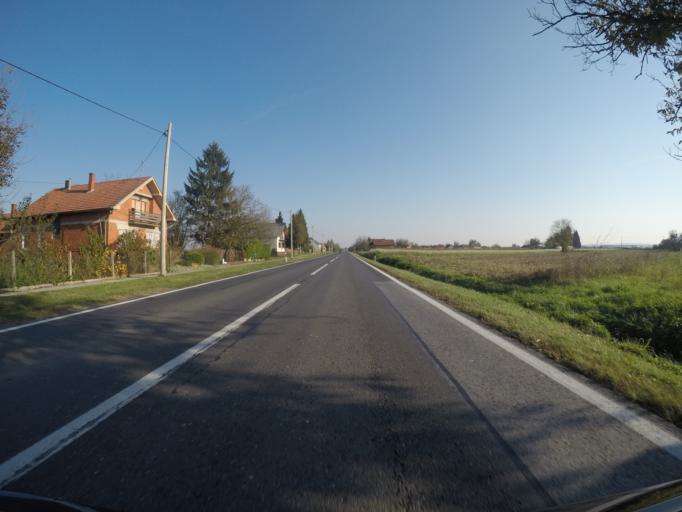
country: HR
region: Koprivnicko-Krizevacka
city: Kalinovac
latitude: 45.9898
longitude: 17.1327
